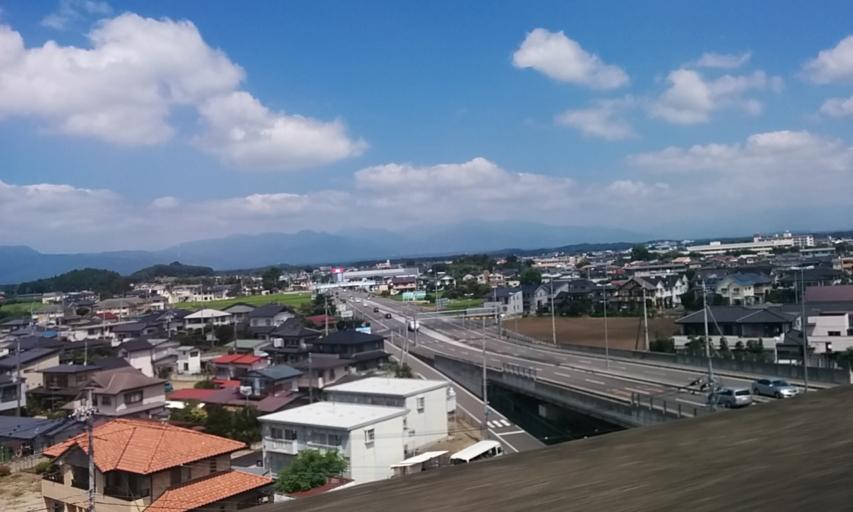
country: JP
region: Tochigi
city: Otawara
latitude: 36.8779
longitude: 139.9820
